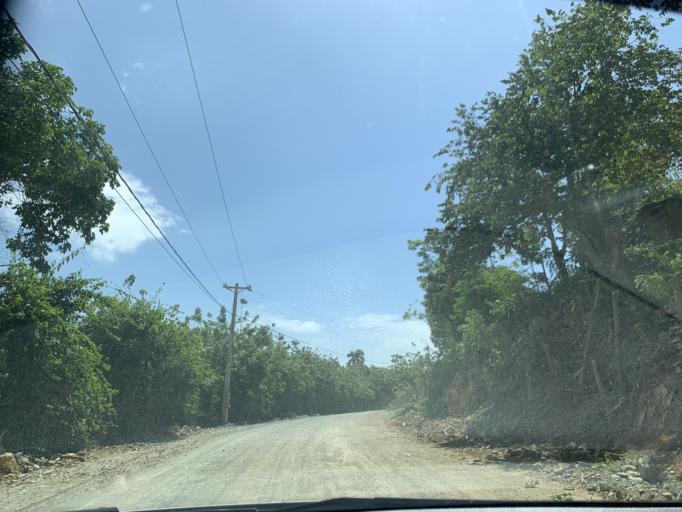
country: DO
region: Puerto Plata
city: Luperon
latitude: 19.8817
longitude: -70.8406
